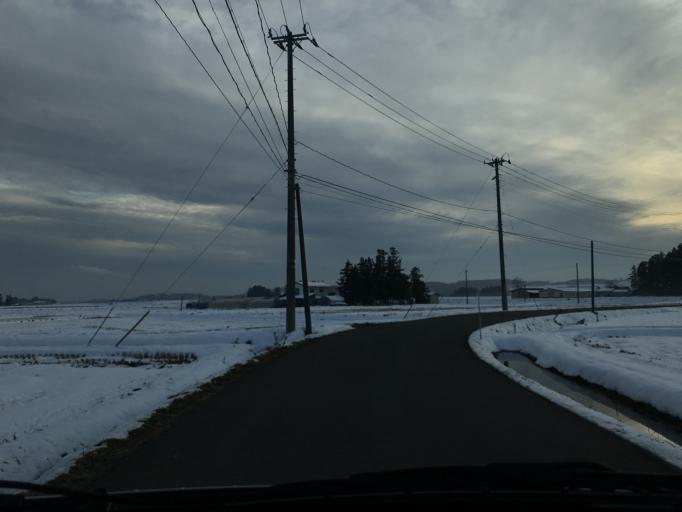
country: JP
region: Iwate
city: Mizusawa
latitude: 39.0632
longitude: 141.0933
